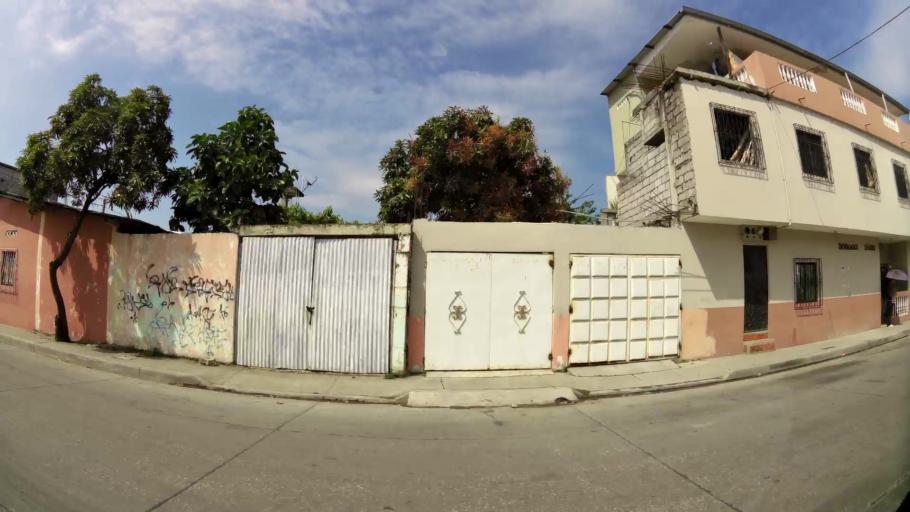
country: EC
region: Guayas
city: Guayaquil
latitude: -2.2651
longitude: -79.8857
